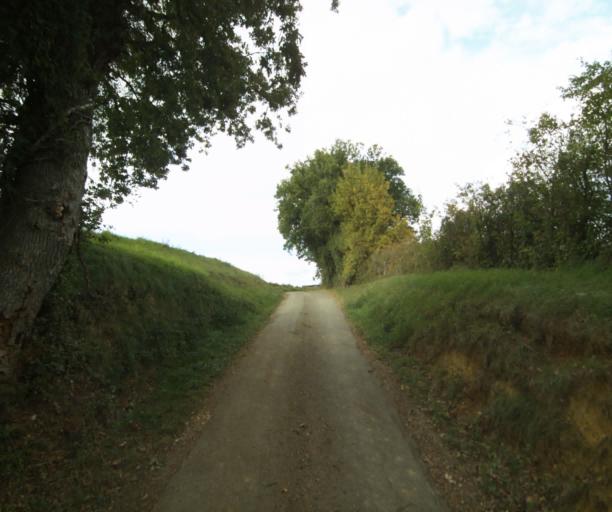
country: FR
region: Midi-Pyrenees
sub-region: Departement du Gers
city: Gondrin
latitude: 43.8593
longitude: 0.2709
